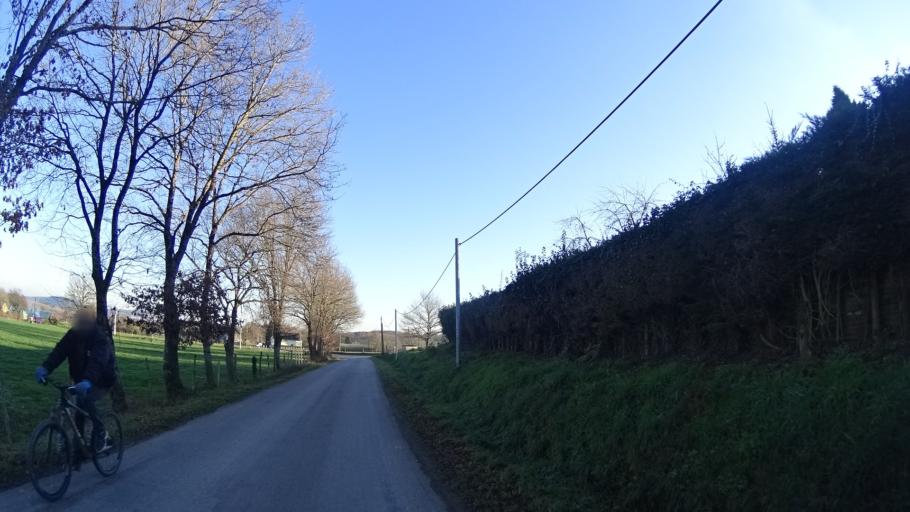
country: FR
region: Brittany
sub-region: Departement du Morbihan
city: Saint-Jean-la-Poterie
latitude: 47.6627
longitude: -2.1419
